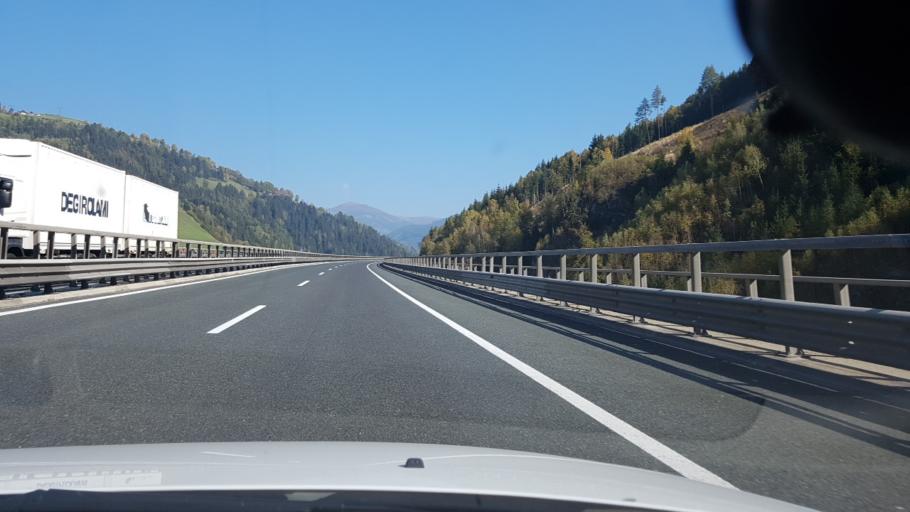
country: AT
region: Carinthia
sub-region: Politischer Bezirk Spittal an der Drau
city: Gmuend
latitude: 46.9140
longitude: 13.5596
